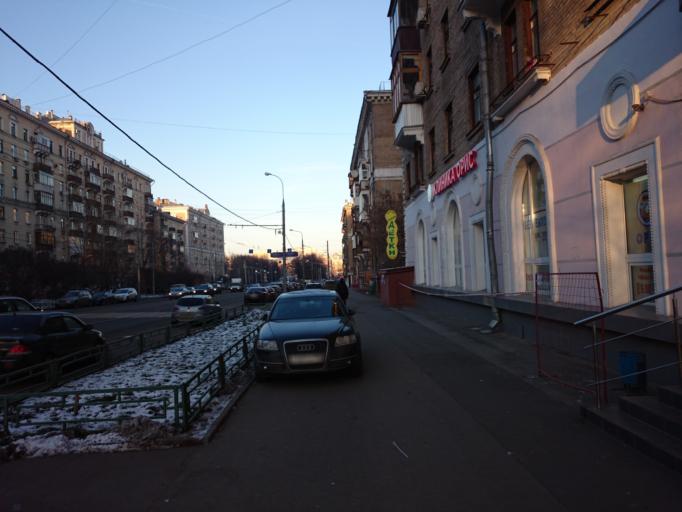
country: RU
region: Moscow
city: Sokol
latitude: 55.7946
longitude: 37.5116
